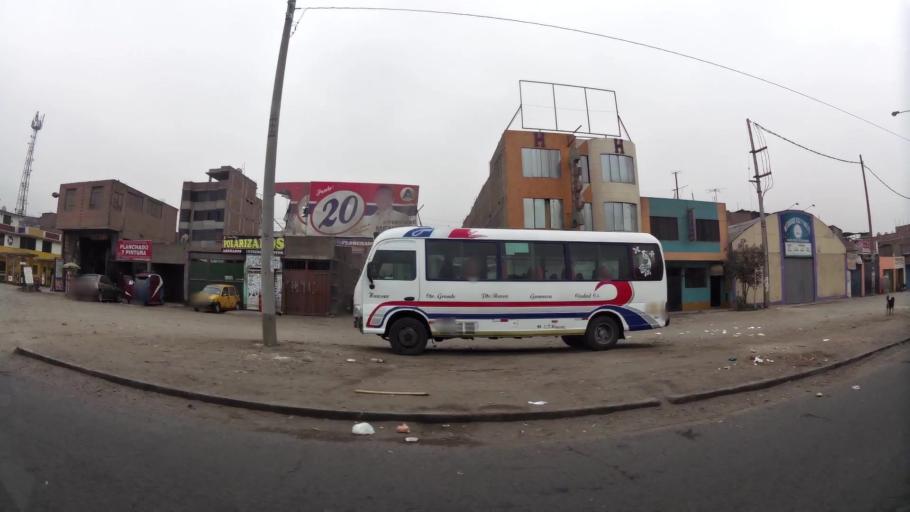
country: PE
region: Lima
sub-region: Lima
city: Independencia
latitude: -11.9527
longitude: -76.9872
